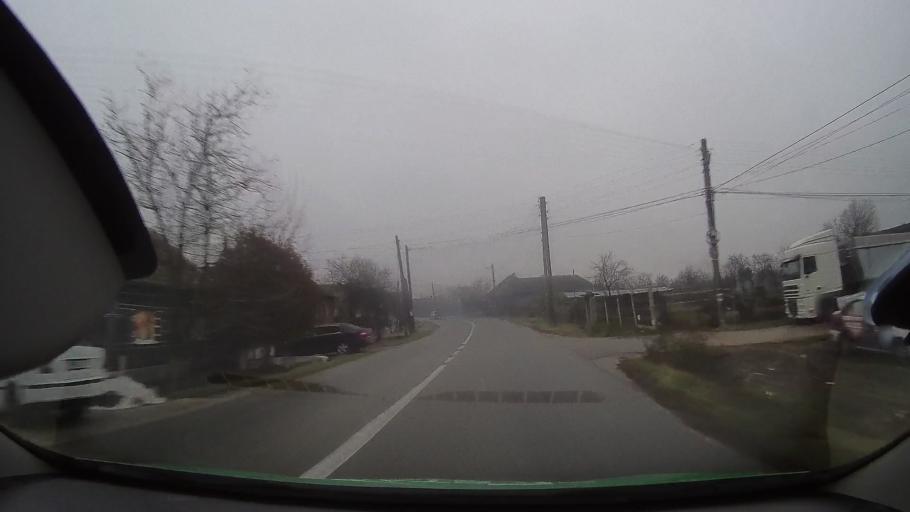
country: RO
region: Bihor
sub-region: Comuna Tulca
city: Tulca
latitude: 46.7869
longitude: 21.7829
